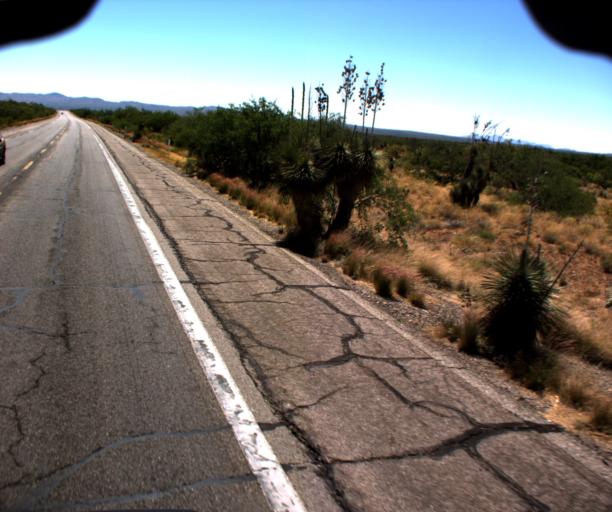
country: US
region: Arizona
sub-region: Pinal County
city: Oracle
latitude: 32.6093
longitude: -110.8500
